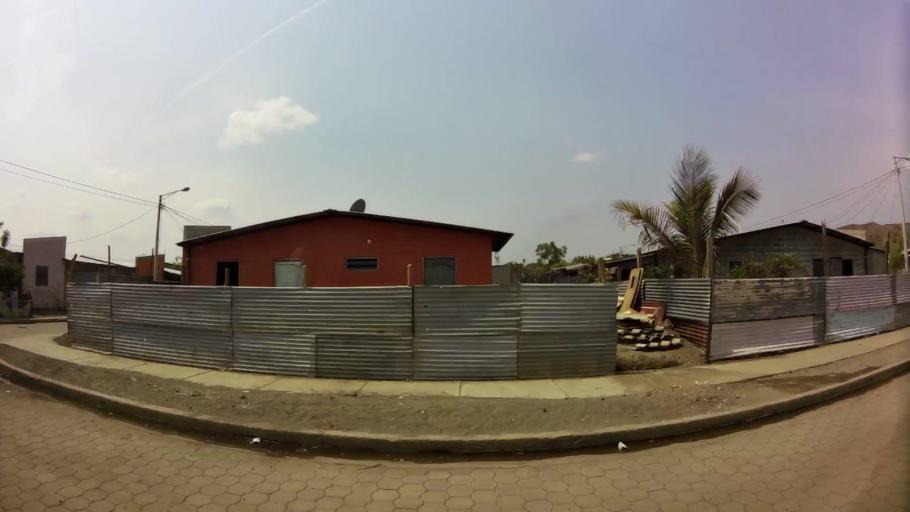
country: NI
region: Managua
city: Ciudad Sandino
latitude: 12.1615
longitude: -86.3120
